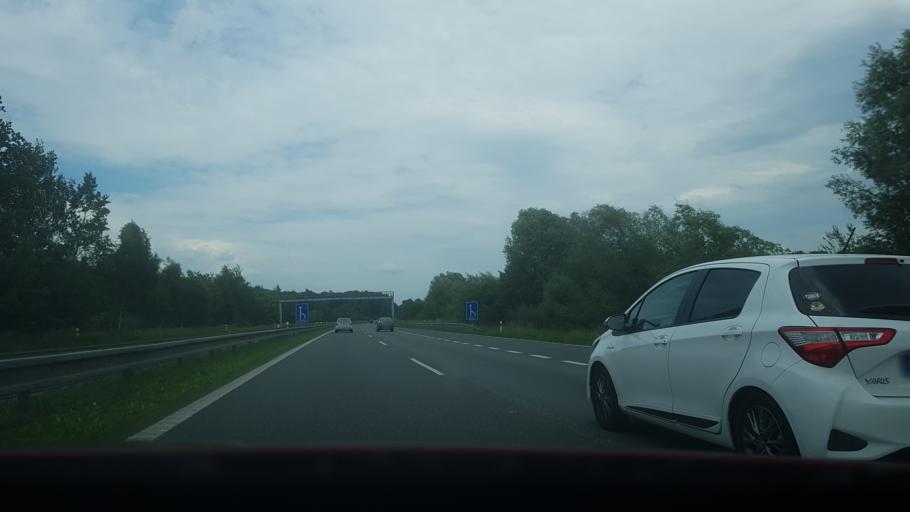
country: CZ
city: Dobra
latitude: 49.6820
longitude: 18.3892
